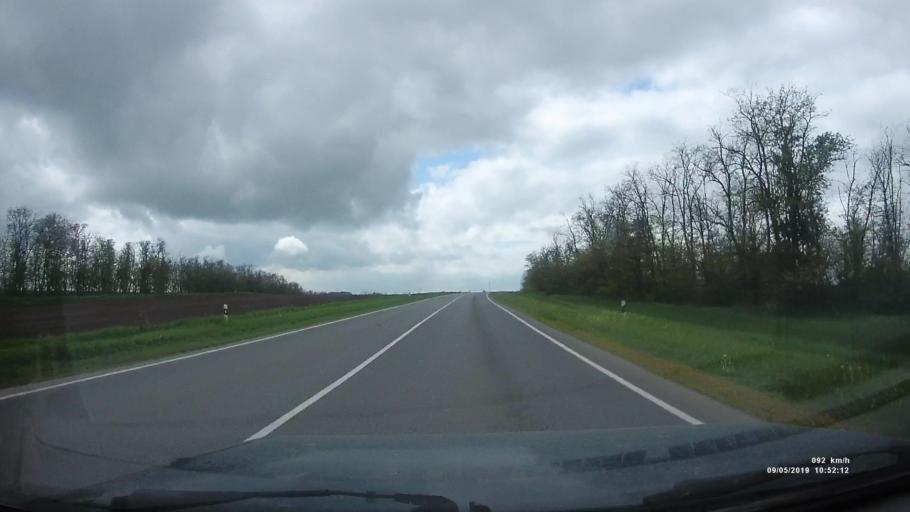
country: RU
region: Rostov
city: Peshkovo
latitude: 46.9038
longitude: 39.3544
